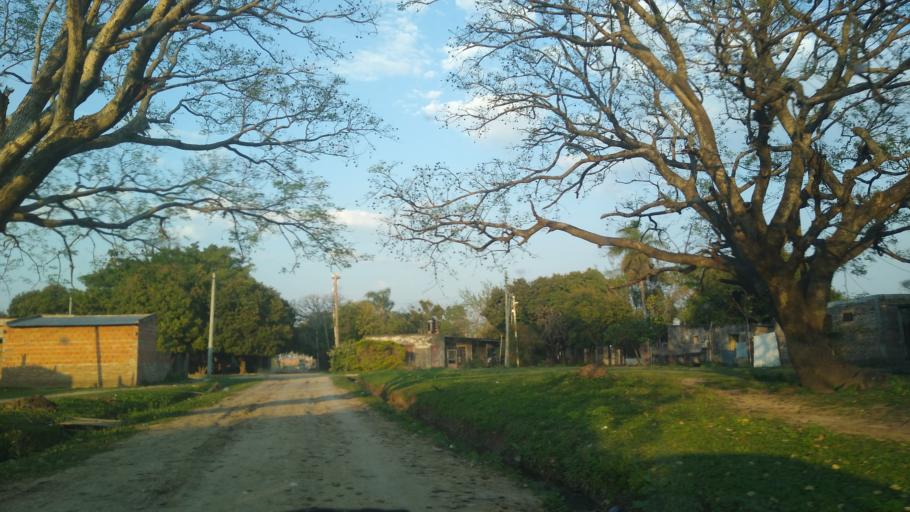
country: AR
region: Chaco
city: Barranqueras
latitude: -27.4706
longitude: -58.9568
